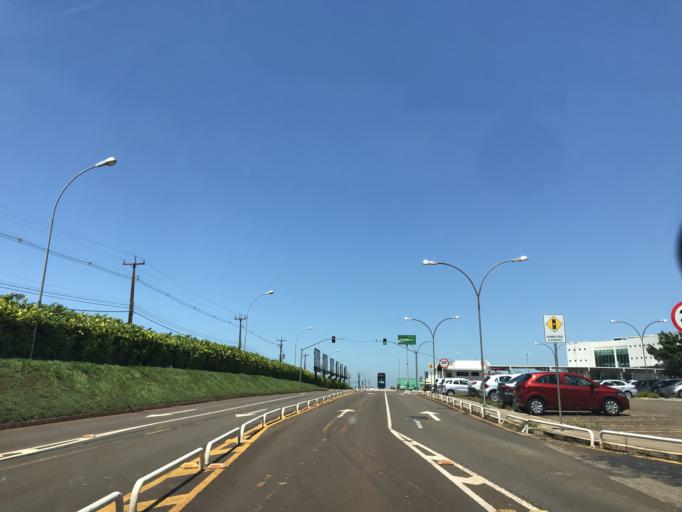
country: BR
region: Parana
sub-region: Paicandu
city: Paicandu
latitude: -23.4799
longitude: -52.0107
